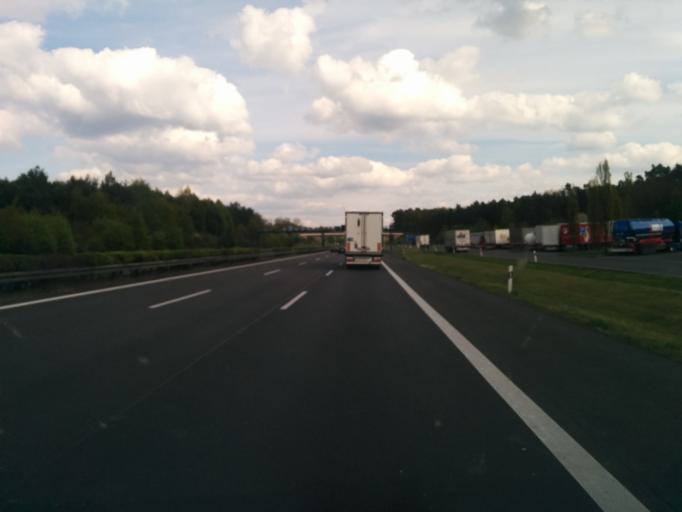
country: DE
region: Brandenburg
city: Fichtenwalde
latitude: 52.3213
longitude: 12.8507
